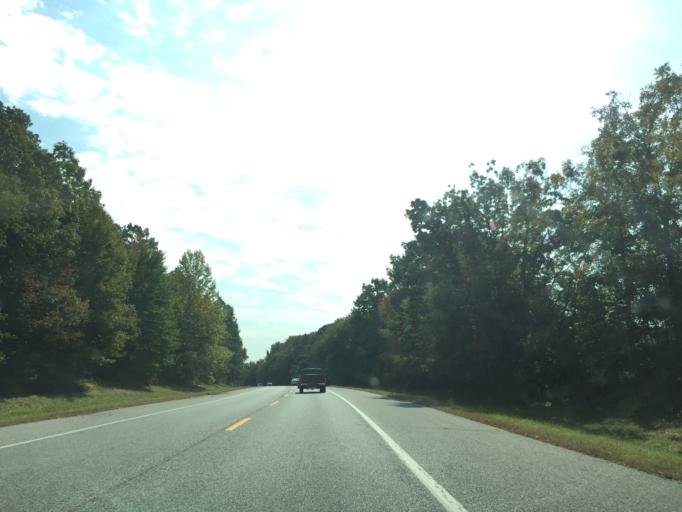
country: US
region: Maryland
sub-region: Harford County
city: Edgewood
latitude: 39.4215
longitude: -76.3098
